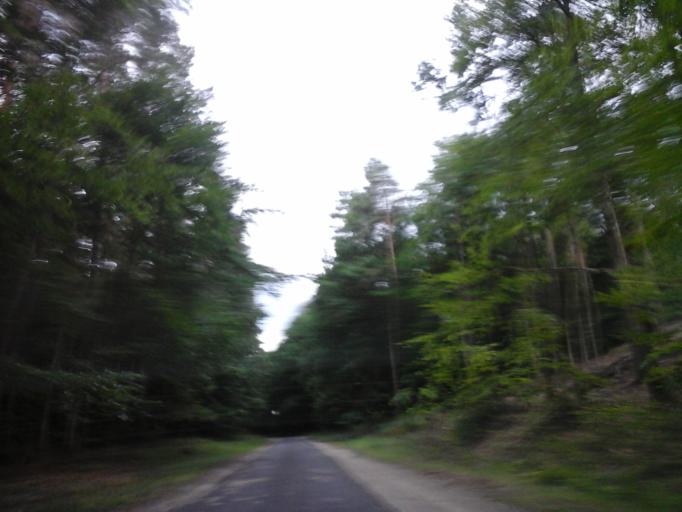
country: PL
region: West Pomeranian Voivodeship
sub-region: Powiat choszczenski
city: Drawno
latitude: 53.1598
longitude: 15.8653
